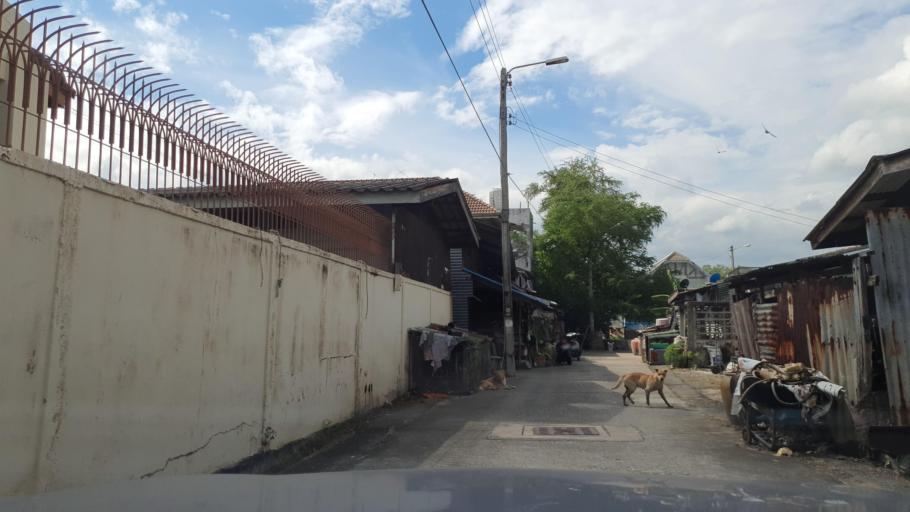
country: TH
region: Chon Buri
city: Chon Buri
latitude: 13.3699
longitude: 100.9805
